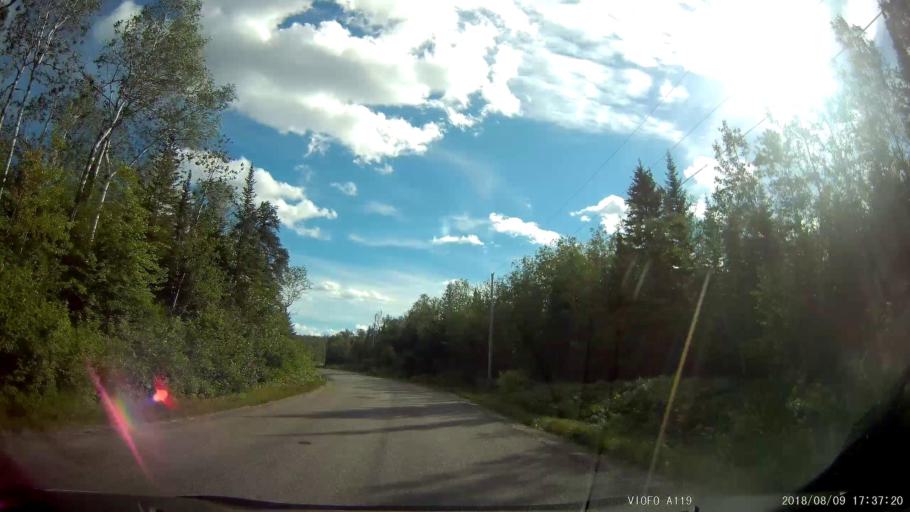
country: CA
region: Ontario
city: Rayside-Balfour
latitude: 46.6101
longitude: -81.4737
